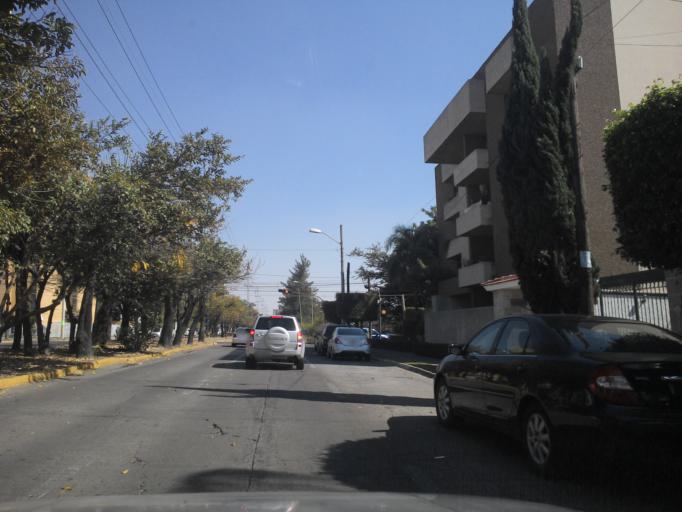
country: MX
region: Jalisco
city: Guadalajara
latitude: 20.6873
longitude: -103.3837
